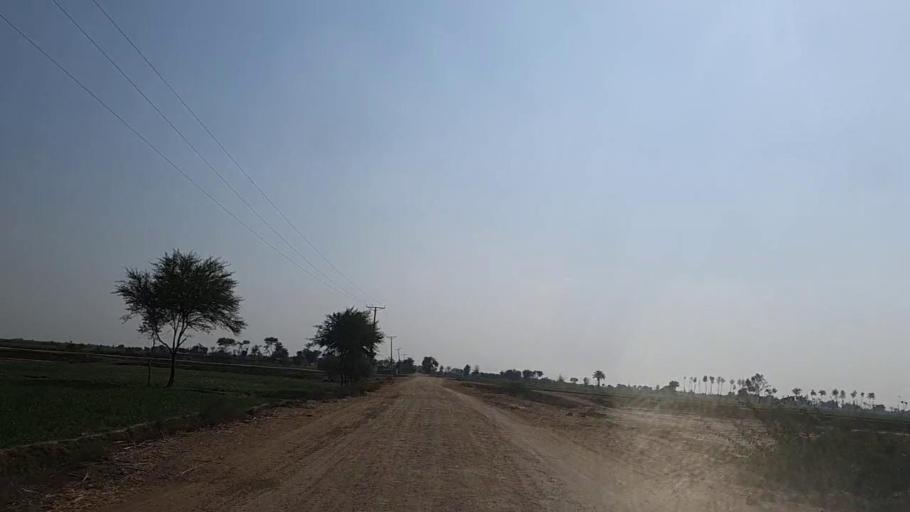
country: PK
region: Sindh
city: Daur
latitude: 26.4590
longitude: 68.2348
